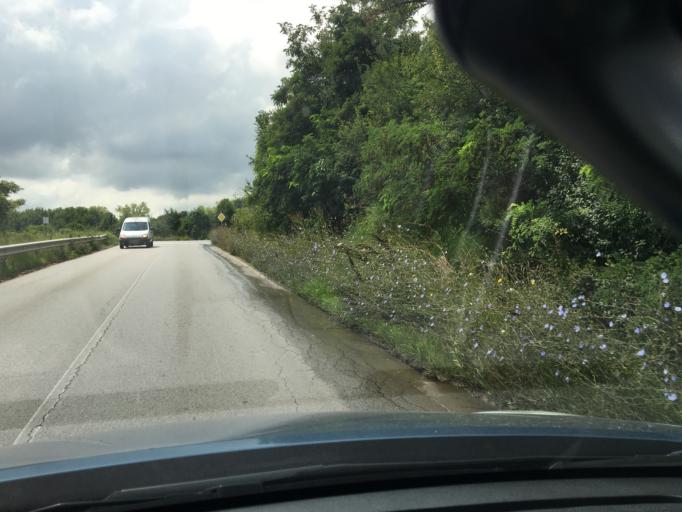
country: BG
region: Sofia-Capital
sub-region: Stolichna Obshtina
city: Sofia
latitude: 42.5990
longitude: 23.3686
